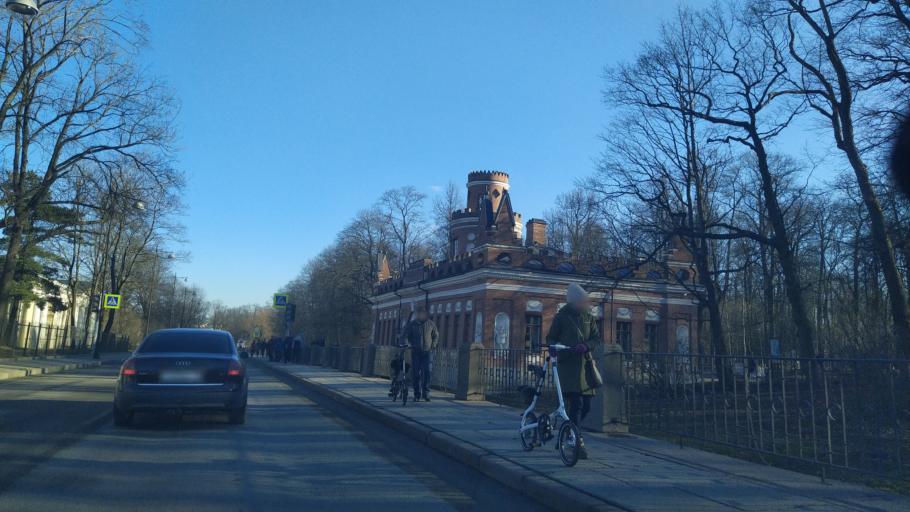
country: RU
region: St.-Petersburg
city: Pushkin
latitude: 59.7150
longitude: 30.4041
